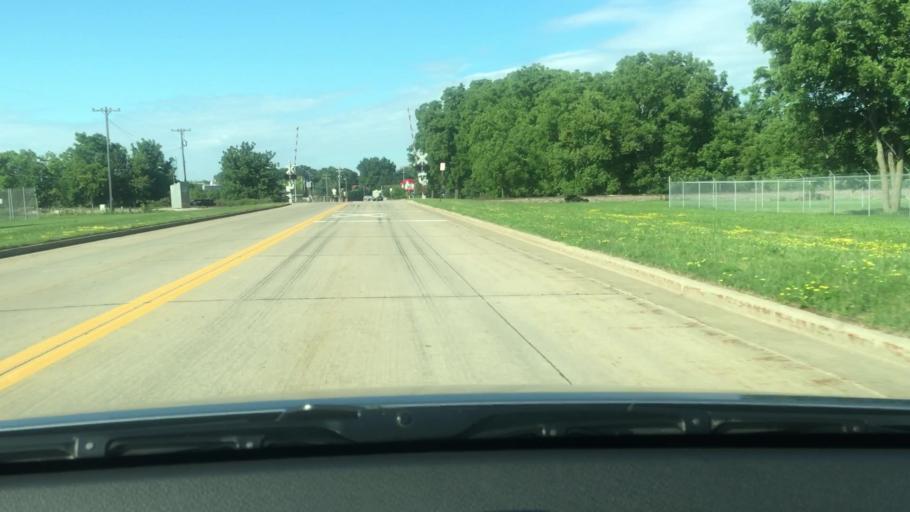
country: US
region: Wisconsin
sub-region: Winnebago County
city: Oshkosh
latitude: 43.9893
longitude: -88.5454
